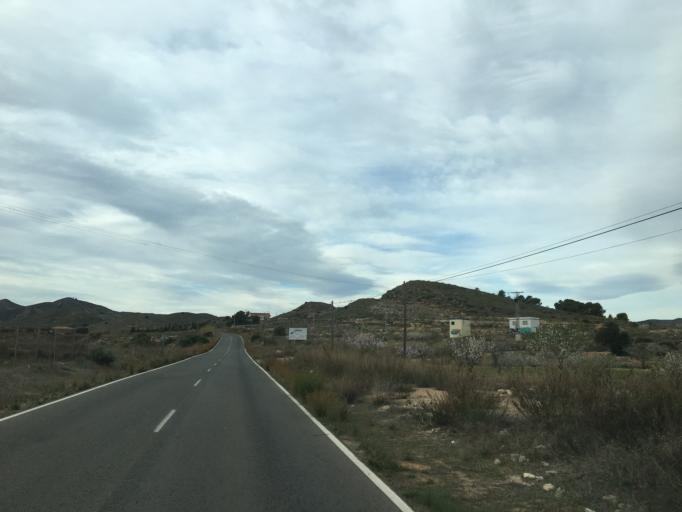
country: ES
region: Murcia
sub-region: Murcia
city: Fuente-Alamo de Murcia
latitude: 37.6167
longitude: -1.0928
